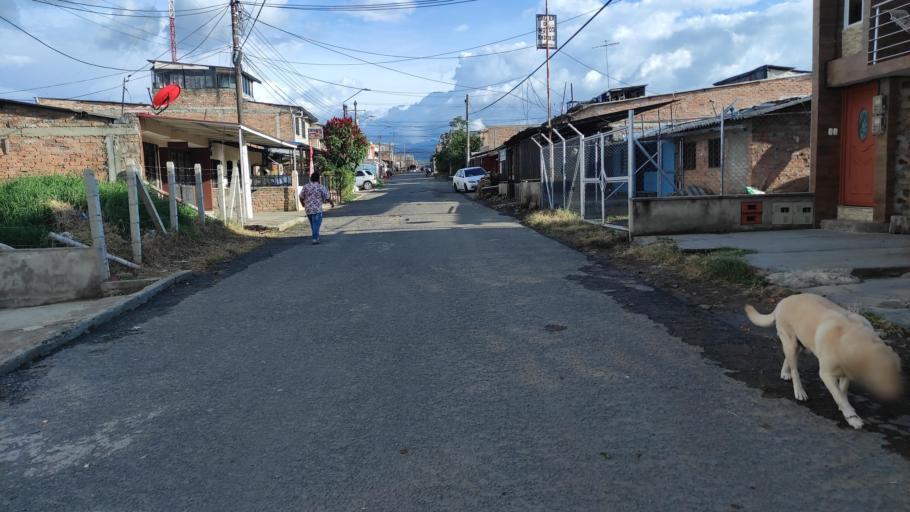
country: CO
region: Cauca
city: Popayan
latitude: 2.4903
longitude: -76.5680
